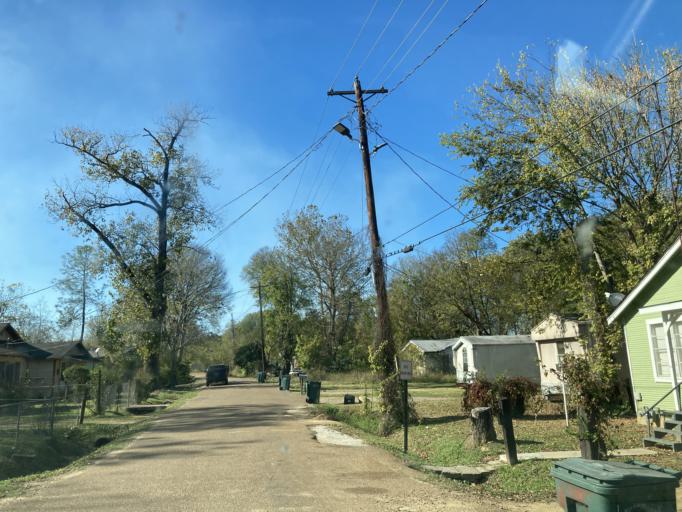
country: US
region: Mississippi
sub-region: Yazoo County
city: Yazoo City
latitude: 32.8532
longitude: -90.4156
